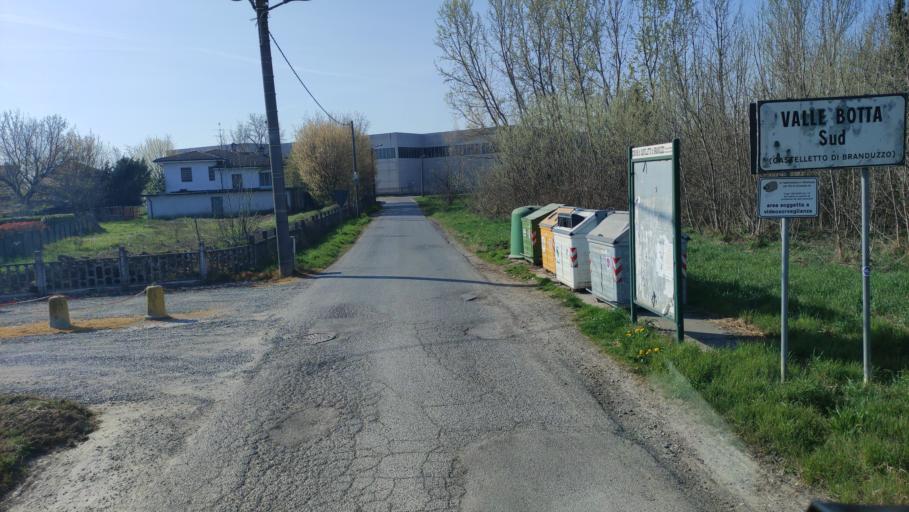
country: IT
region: Lombardy
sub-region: Provincia di Pavia
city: Castelletto Po
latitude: 45.0888
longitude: 9.1100
